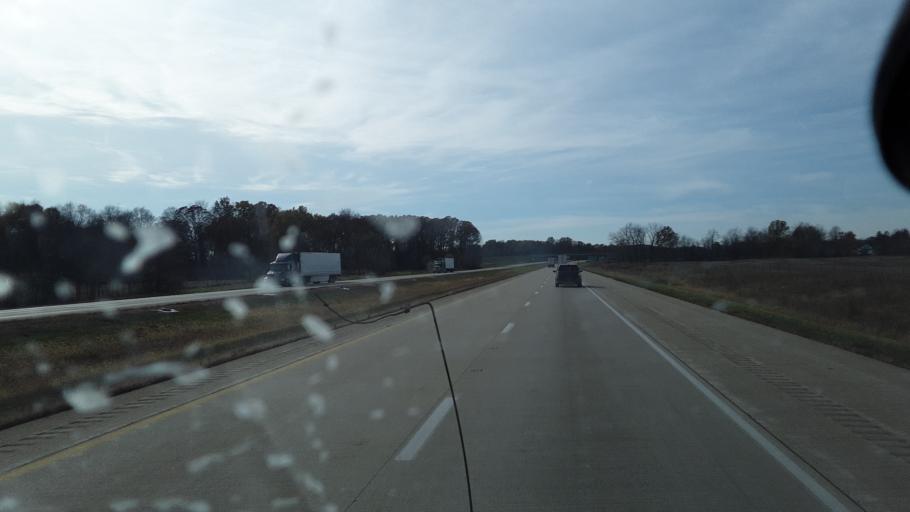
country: US
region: Illinois
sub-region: Clark County
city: Marshall
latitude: 39.4282
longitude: -87.5759
